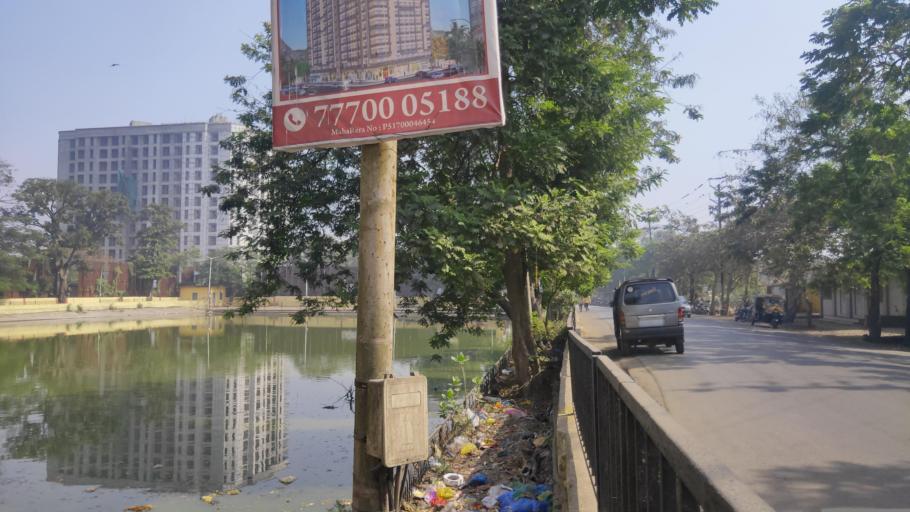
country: IN
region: Maharashtra
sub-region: Thane
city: Bhiwandi
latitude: 19.2831
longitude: 73.0774
